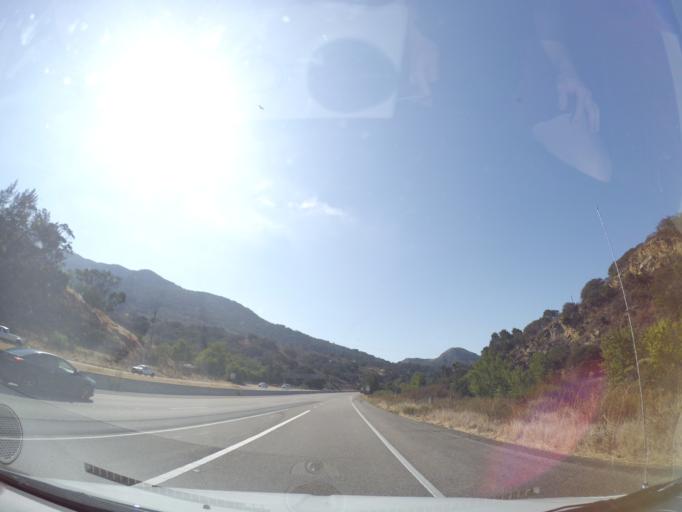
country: US
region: California
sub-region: Santa Barbara County
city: Buellton
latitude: 34.5066
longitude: -120.2266
